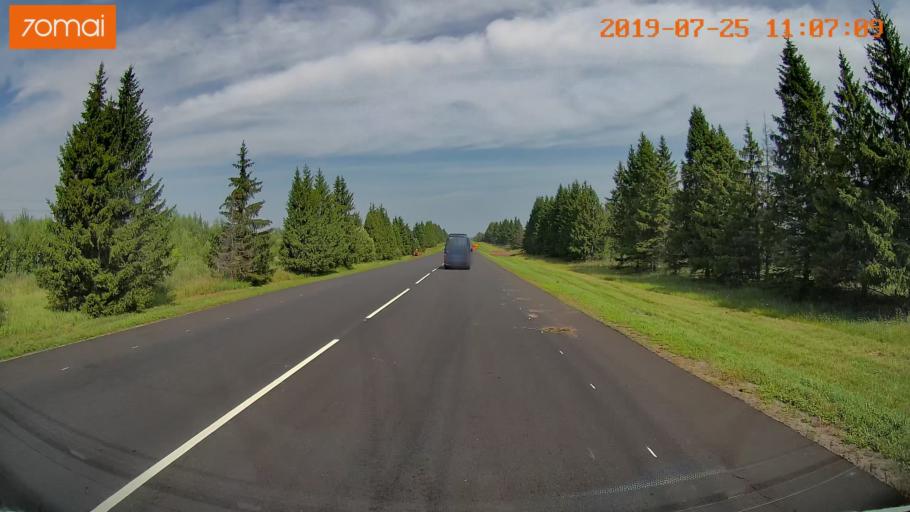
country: RU
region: Ivanovo
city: Furmanov
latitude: 57.2644
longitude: 41.1573
